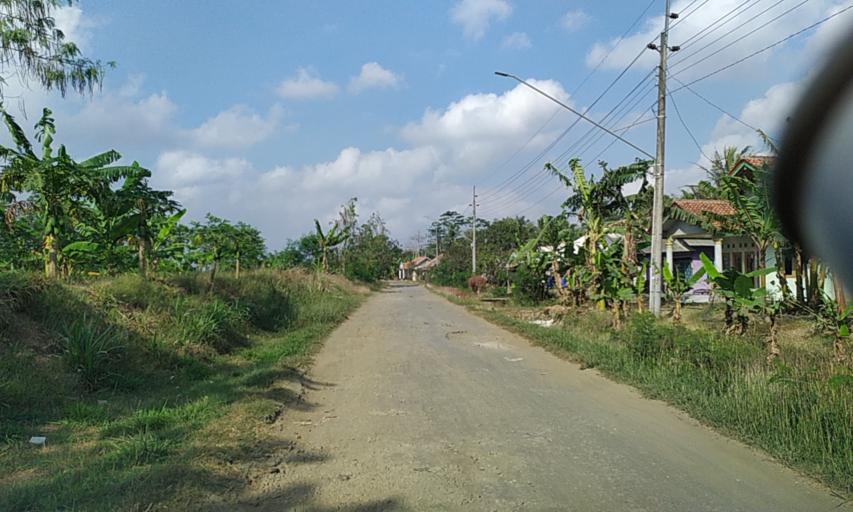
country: ID
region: Central Java
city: Sidakaya
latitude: -7.6142
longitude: 108.8616
